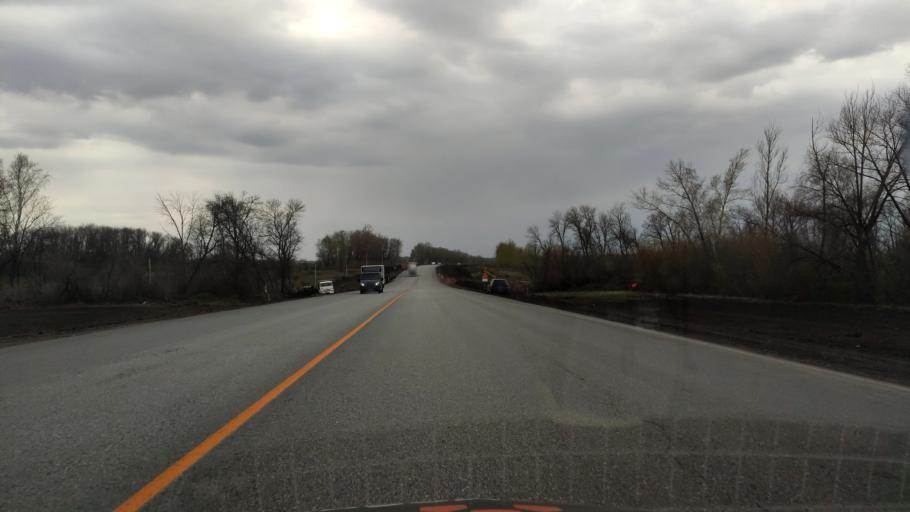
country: RU
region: Kursk
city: Gorshechnoye
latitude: 51.5473
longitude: 38.0711
